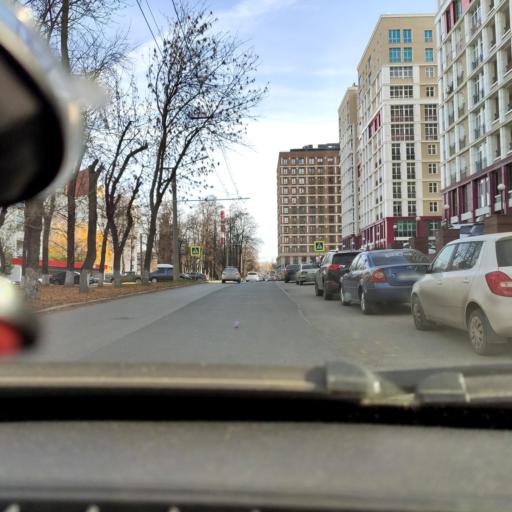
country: RU
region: Bashkortostan
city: Ufa
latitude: 54.7435
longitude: 55.9528
